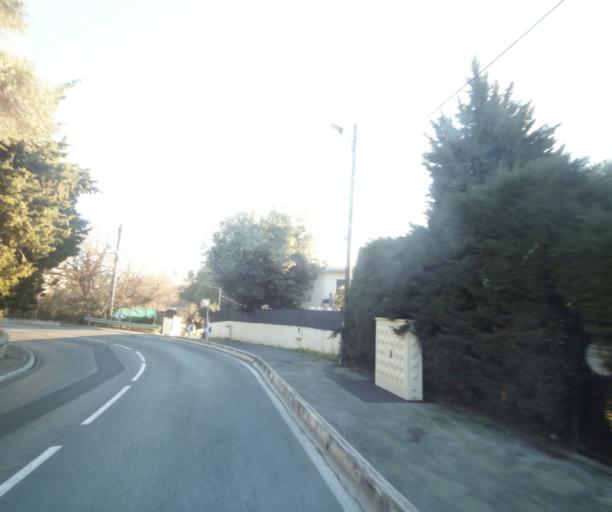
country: FR
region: Provence-Alpes-Cote d'Azur
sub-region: Departement des Alpes-Maritimes
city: Antibes
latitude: 43.5757
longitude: 7.1004
